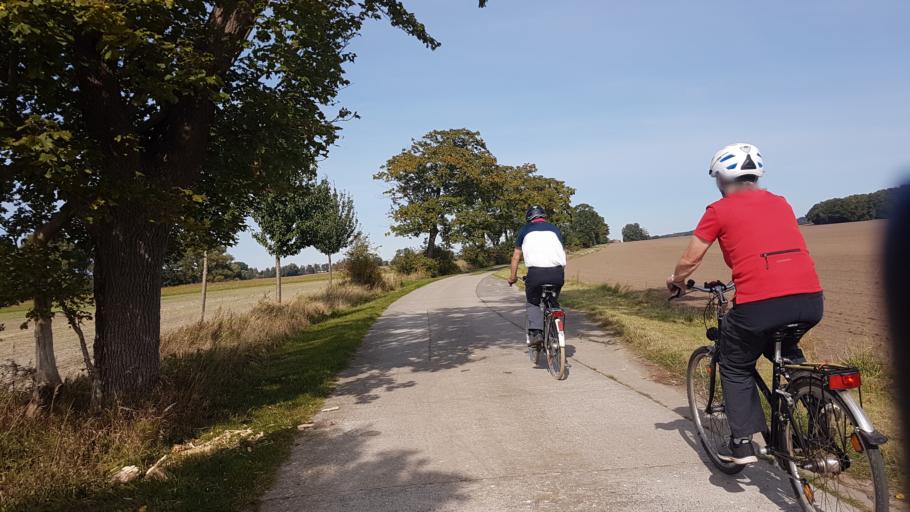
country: DE
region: Mecklenburg-Vorpommern
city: Gingst
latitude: 54.4083
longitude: 13.2561
